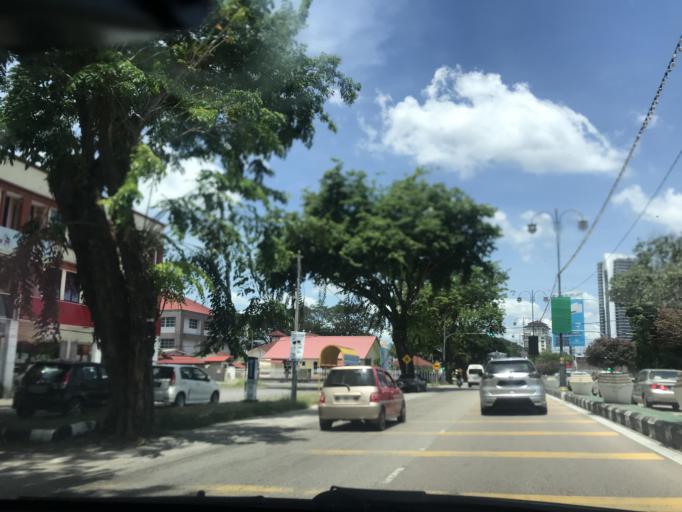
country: MY
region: Kelantan
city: Kota Bharu
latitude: 6.1266
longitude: 102.2421
